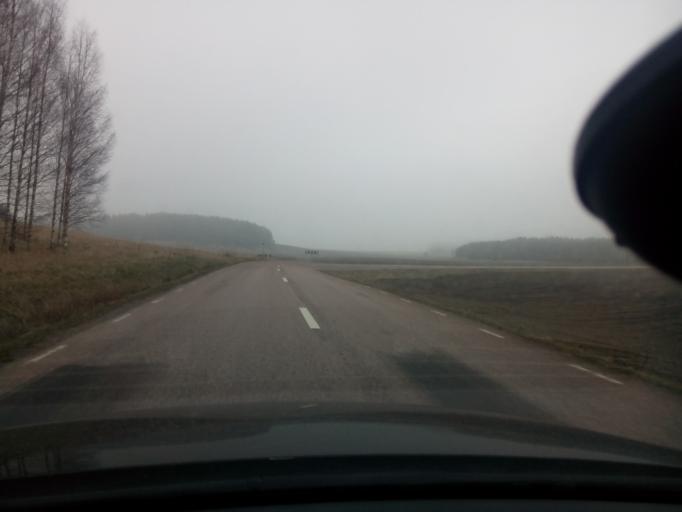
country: SE
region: Soedermanland
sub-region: Nykopings Kommun
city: Nykoping
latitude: 58.9064
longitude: 17.0985
